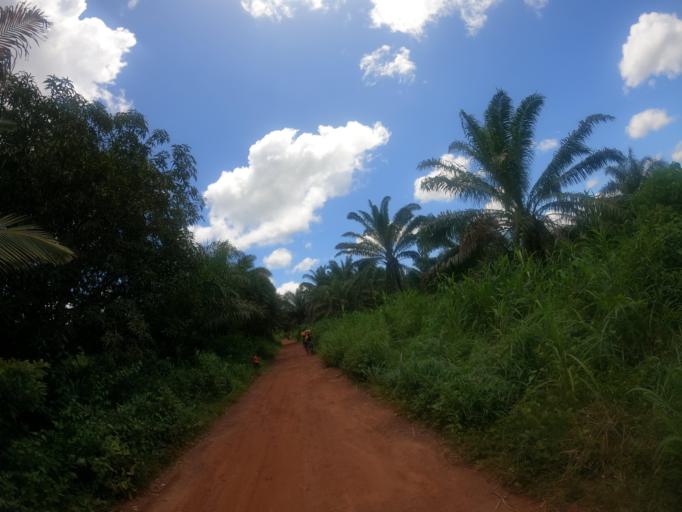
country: SL
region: Northern Province
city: Makeni
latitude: 8.8658
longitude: -12.1063
